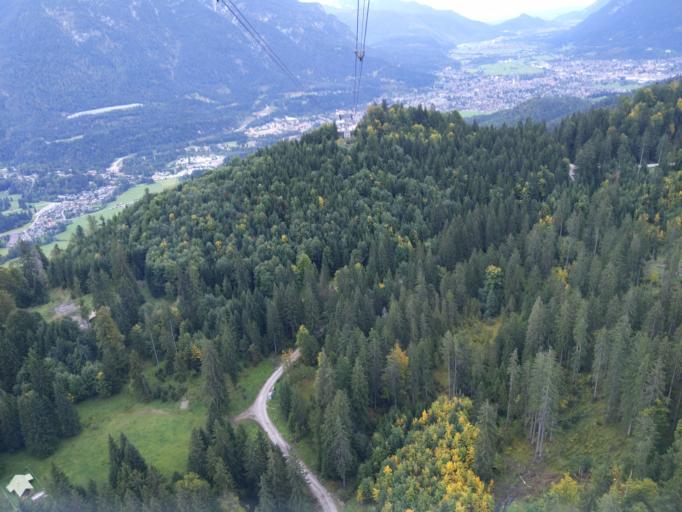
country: DE
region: Bavaria
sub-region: Upper Bavaria
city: Grainau
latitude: 47.4560
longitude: 11.0565
